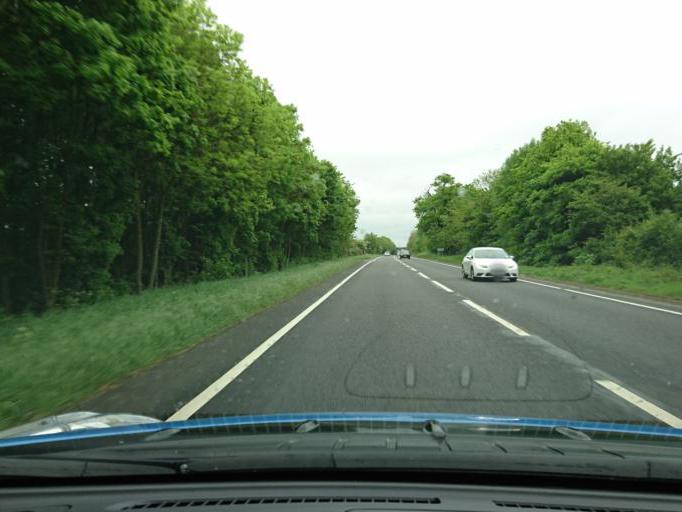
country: GB
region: England
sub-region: Oxfordshire
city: Shrivenham
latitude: 51.5990
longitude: -1.6678
